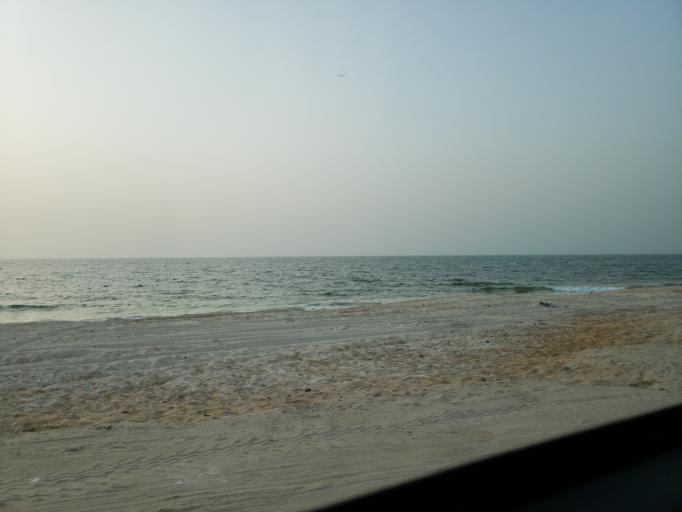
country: AE
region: Ajman
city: Ajman
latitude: 25.4277
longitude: 55.4527
